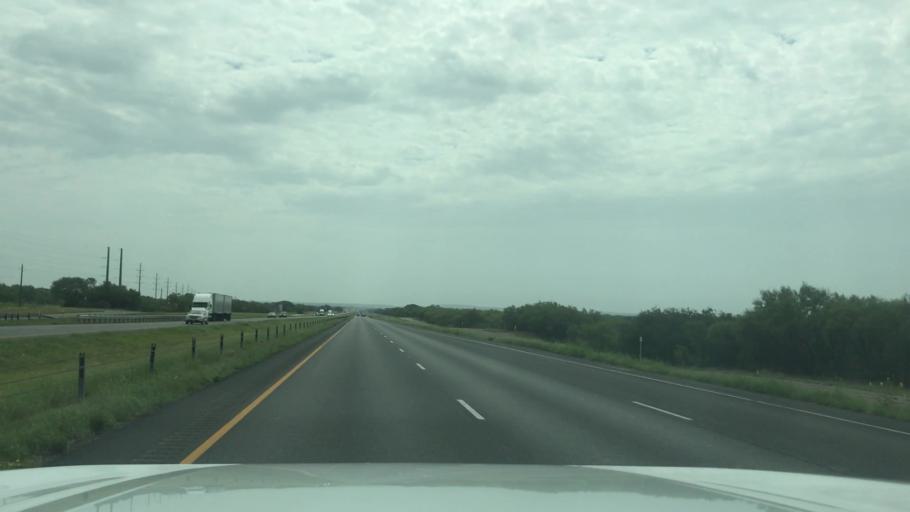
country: US
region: Texas
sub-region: Callahan County
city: Baird
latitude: 32.3909
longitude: -99.3408
